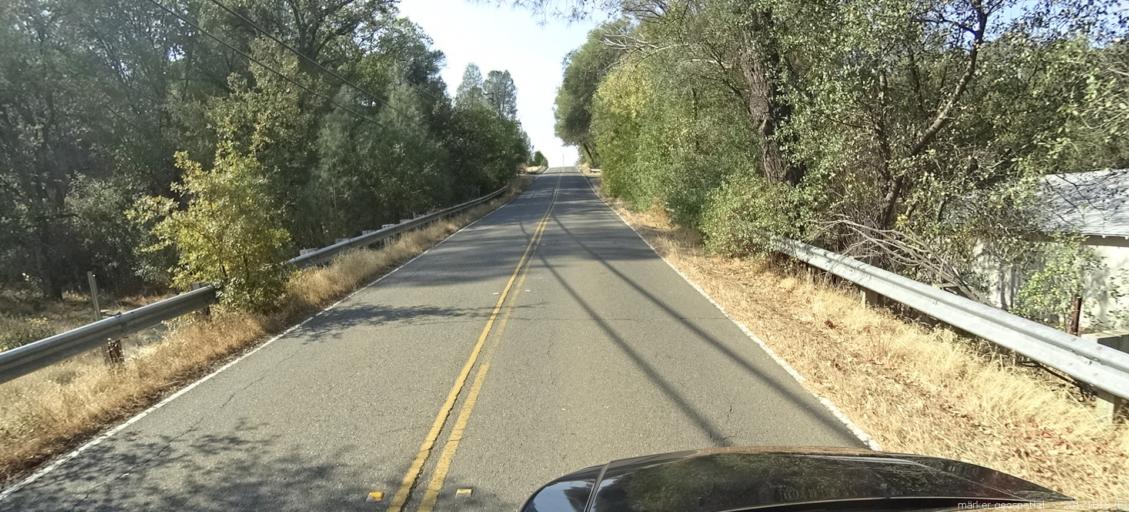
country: US
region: California
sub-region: Shasta County
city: Palo Cedro
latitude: 40.5633
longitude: -122.2920
